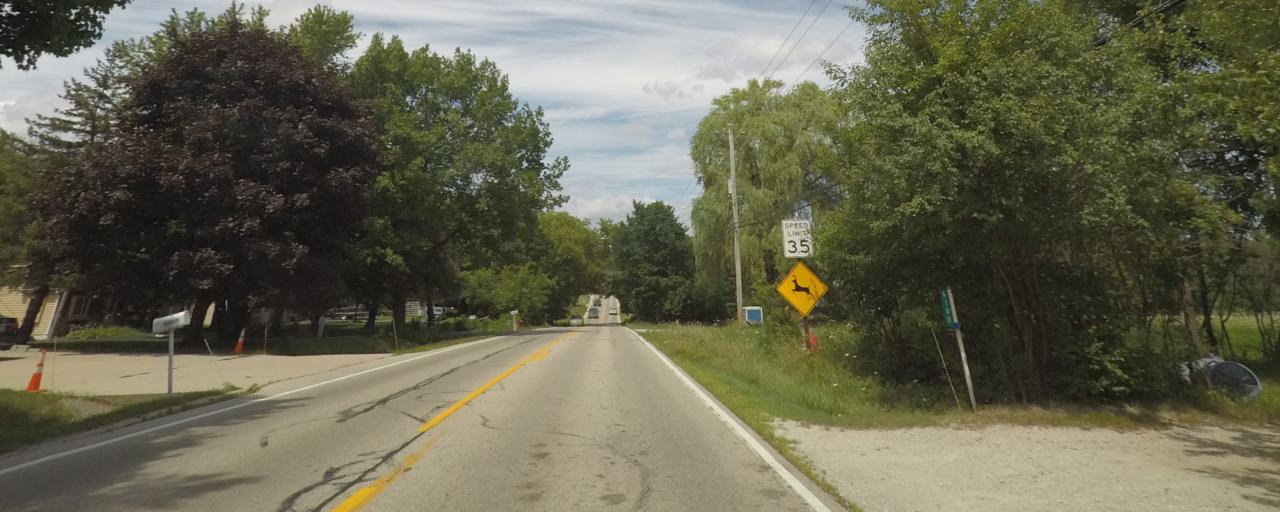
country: US
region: Wisconsin
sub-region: Milwaukee County
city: Hales Corners
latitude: 42.9701
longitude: -88.0690
